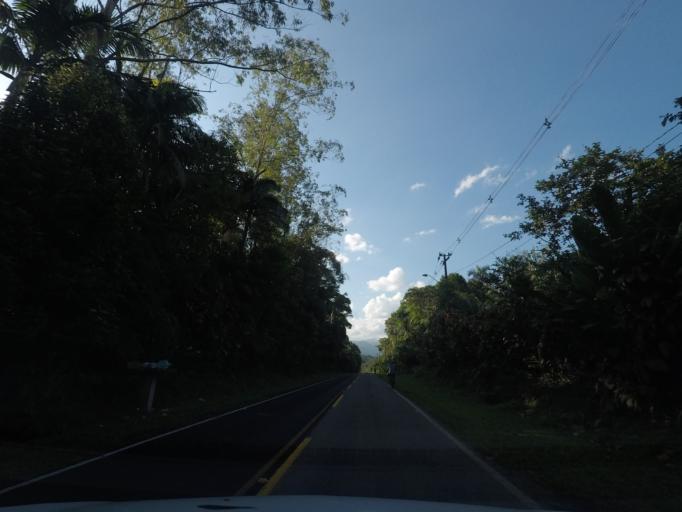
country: BR
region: Parana
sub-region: Antonina
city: Antonina
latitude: -25.4150
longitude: -48.8737
